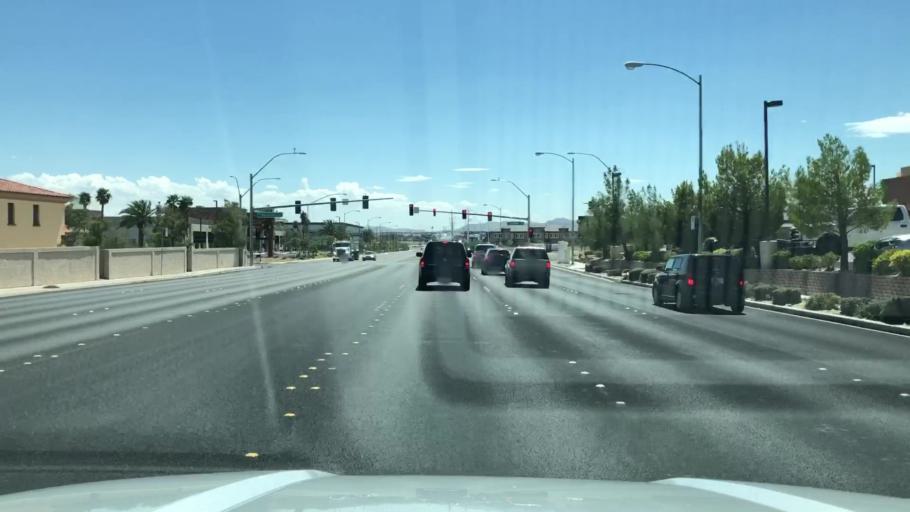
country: US
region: Nevada
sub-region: Clark County
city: Spring Valley
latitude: 36.0936
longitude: -115.2793
